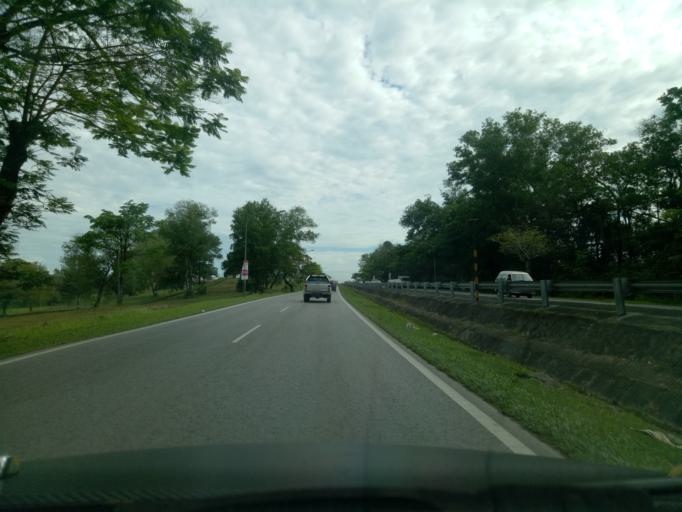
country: MY
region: Sarawak
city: Kuching
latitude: 1.4520
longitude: 110.3259
